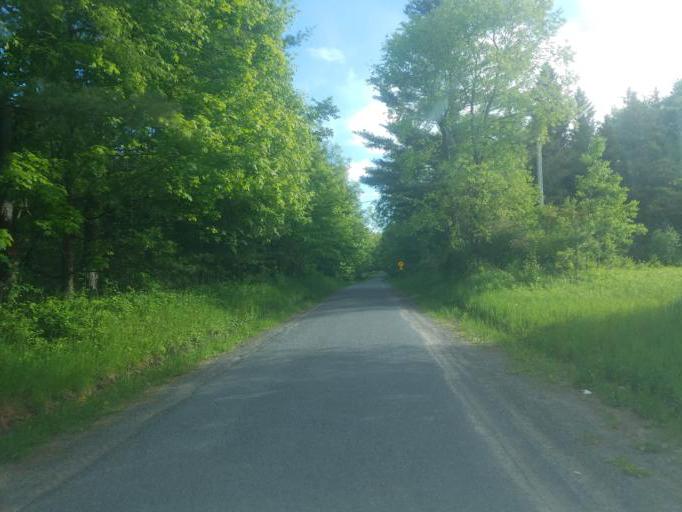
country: US
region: New York
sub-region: Herkimer County
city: Dolgeville
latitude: 43.3234
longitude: -74.9433
